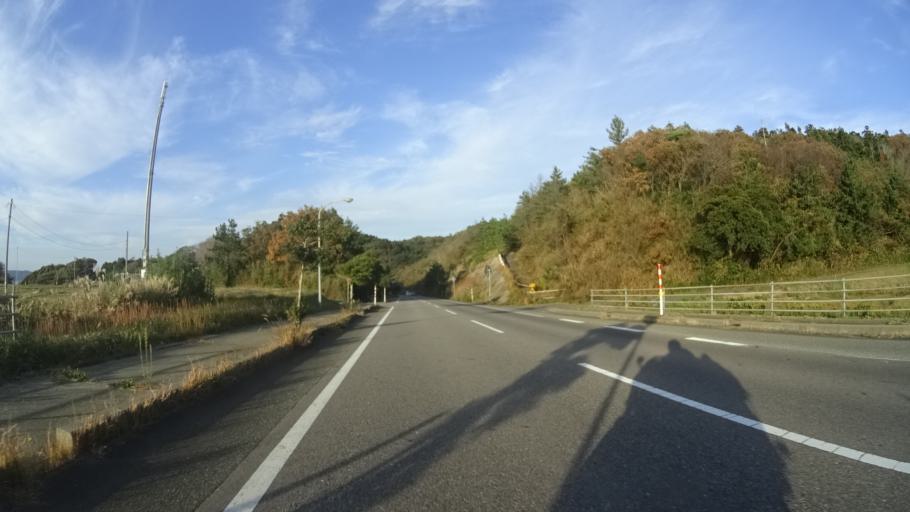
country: JP
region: Ishikawa
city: Hakui
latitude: 37.1153
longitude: 136.7285
